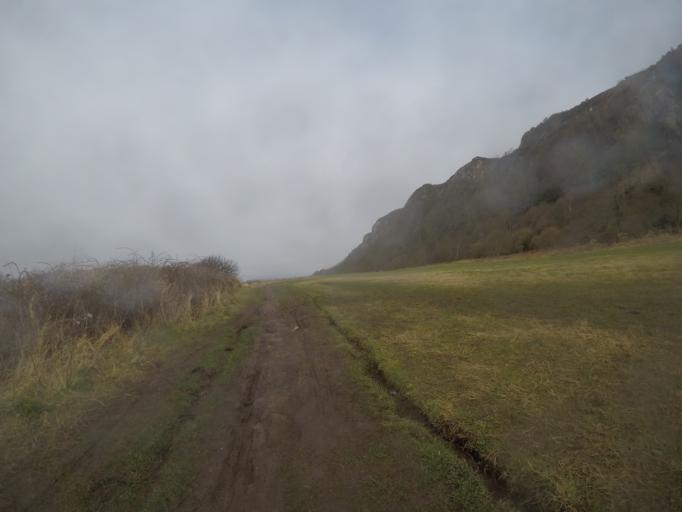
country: GB
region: Scotland
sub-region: North Ayrshire
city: Millport
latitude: 55.7065
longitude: -4.9041
